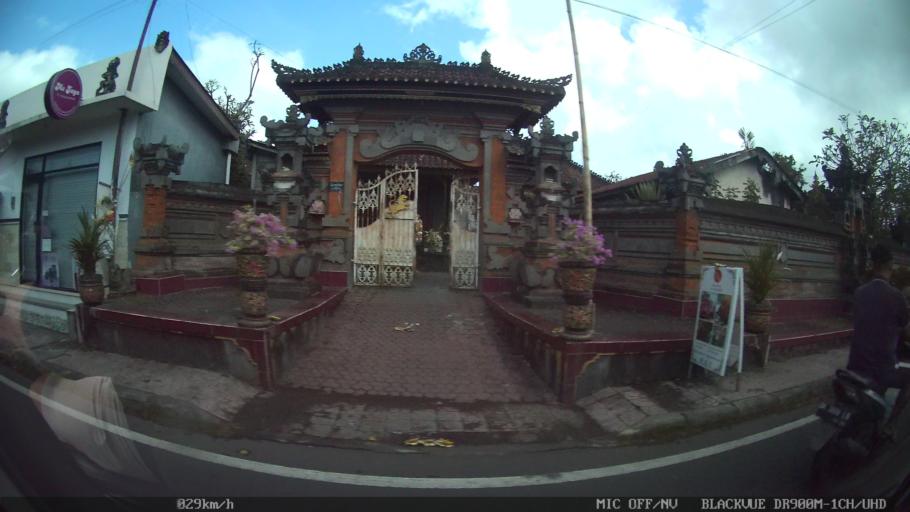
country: ID
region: Bali
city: Banjar Pasekan
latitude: -8.5950
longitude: 115.2844
